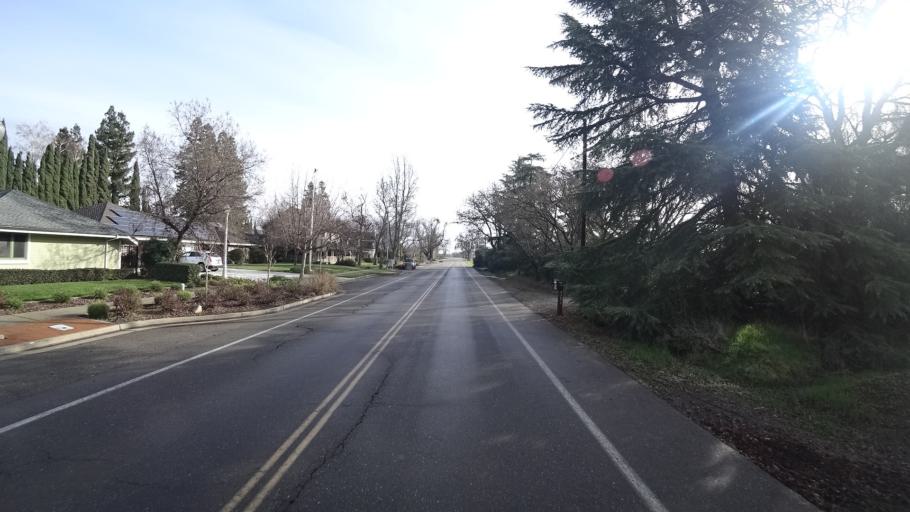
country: US
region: California
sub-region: Yolo County
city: Davis
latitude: 38.5387
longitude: -121.7015
